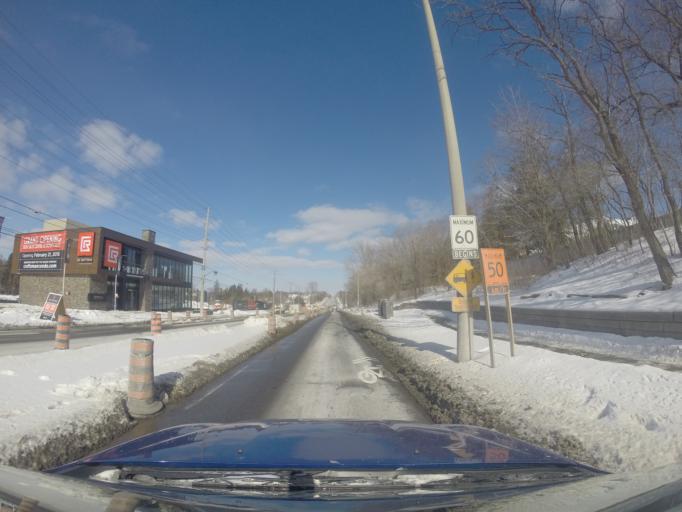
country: CA
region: Ontario
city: Mississauga
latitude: 43.5195
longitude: -79.6206
